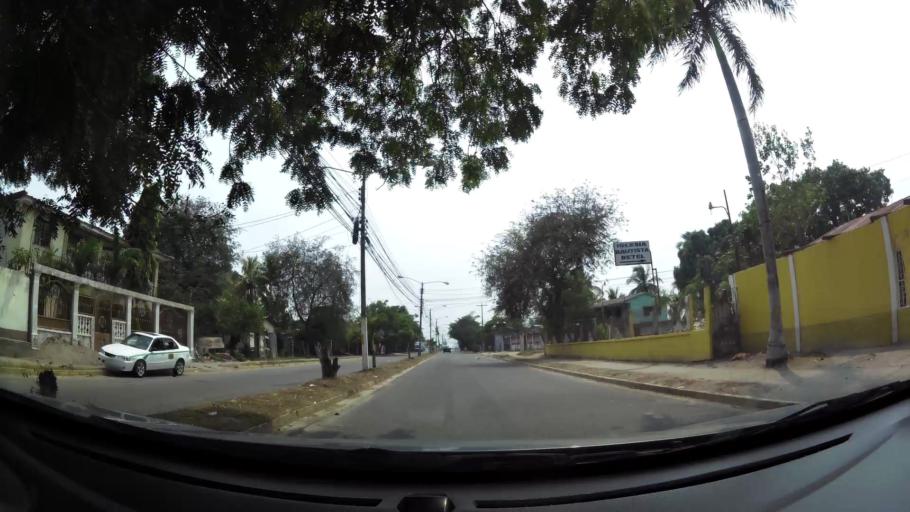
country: HN
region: Cortes
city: La Lima
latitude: 15.4366
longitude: -87.9338
